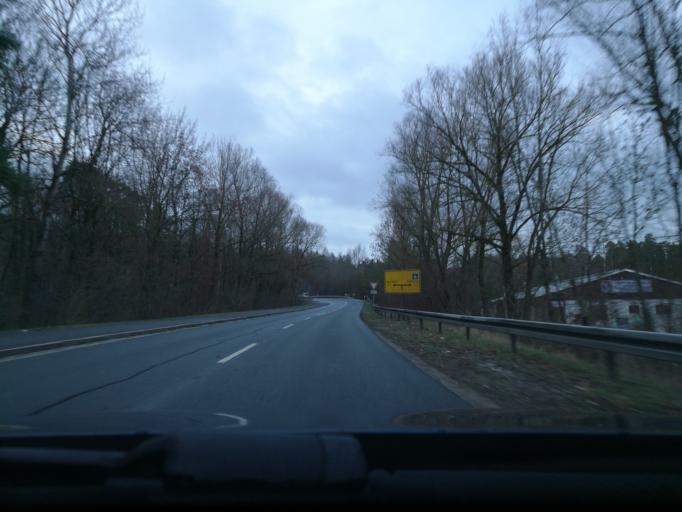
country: DE
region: Bavaria
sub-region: Regierungsbezirk Mittelfranken
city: Heroldsberg
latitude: 49.5219
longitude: 11.1504
